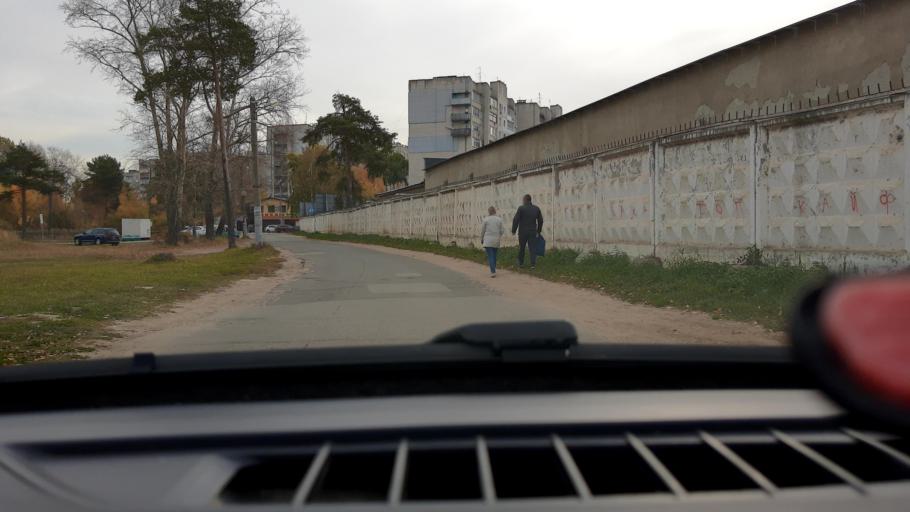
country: RU
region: Nizjnij Novgorod
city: Gorbatovka
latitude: 56.2926
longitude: 43.8380
